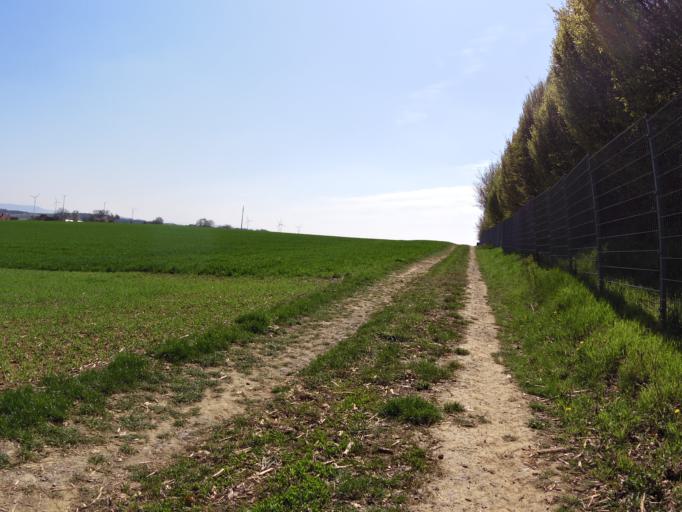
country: DE
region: Bavaria
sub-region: Regierungsbezirk Unterfranken
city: Biebelried
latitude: 49.7830
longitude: 10.0702
